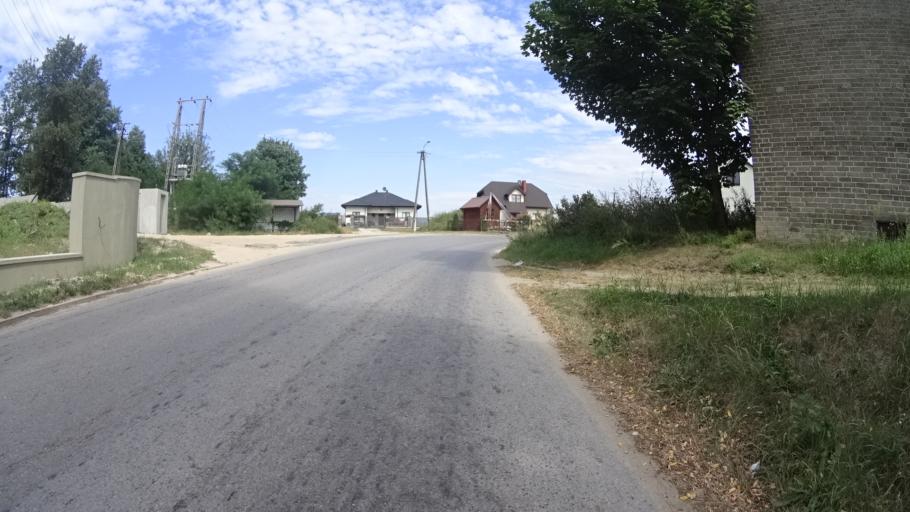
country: PL
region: Masovian Voivodeship
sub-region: Powiat bialobrzeski
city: Wysmierzyce
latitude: 51.6564
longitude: 20.8231
